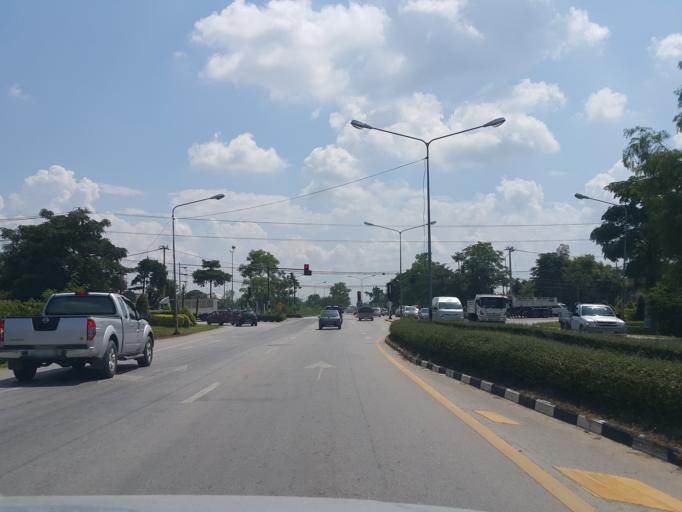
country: TH
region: Chiang Mai
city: San Sai
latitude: 18.8271
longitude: 99.0472
